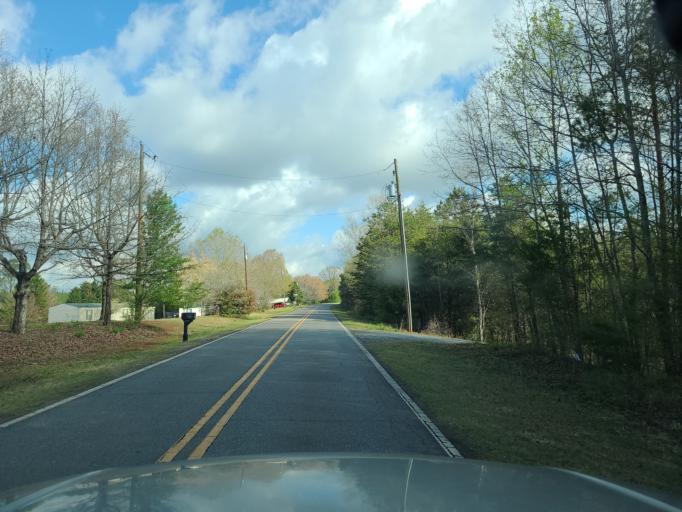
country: US
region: North Carolina
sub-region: Rutherford County
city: Forest City
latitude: 35.4318
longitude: -81.8318
